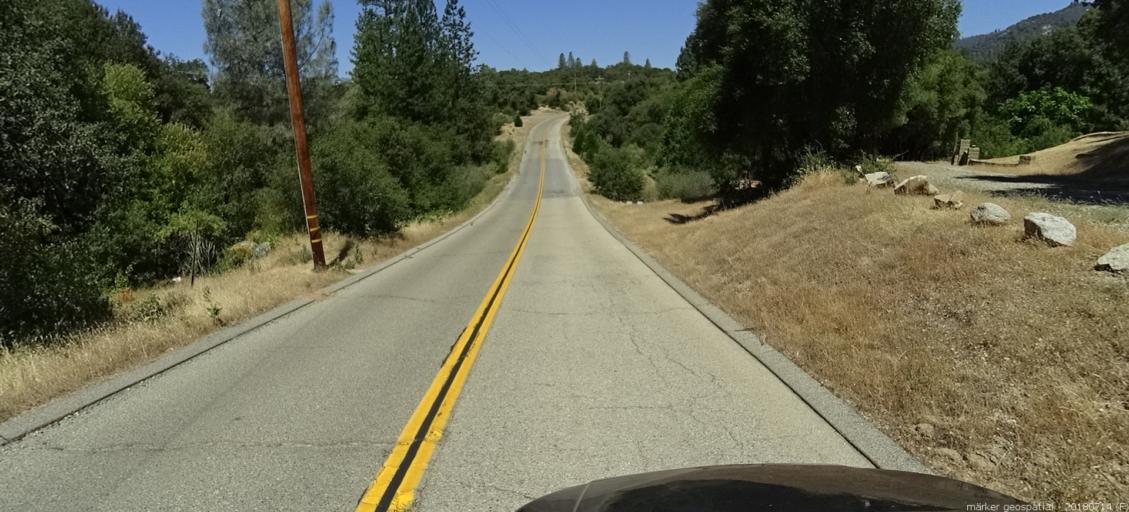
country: US
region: California
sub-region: Madera County
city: Oakhurst
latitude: 37.3753
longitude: -119.6675
